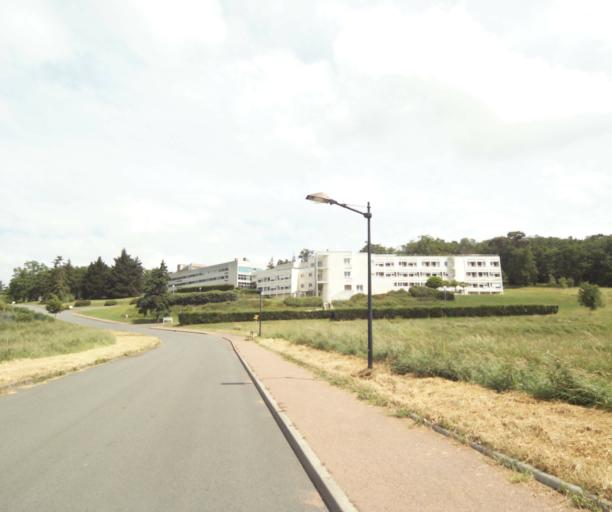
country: FR
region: Pays de la Loire
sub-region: Departement de la Sarthe
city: Solesmes
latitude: 47.8404
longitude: -0.3135
